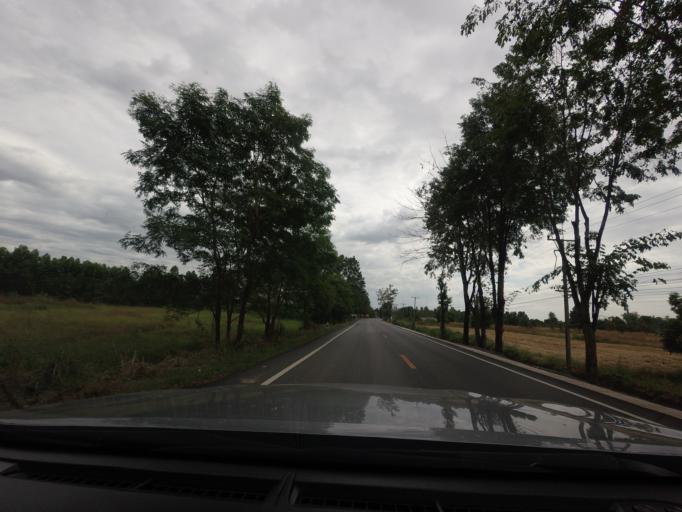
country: TH
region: Phitsanulok
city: Noen Maprang
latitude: 16.6826
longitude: 100.6030
